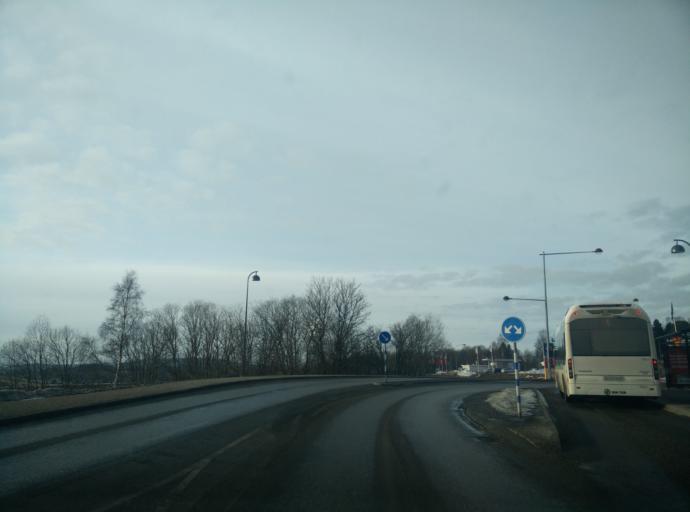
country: SE
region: Vaesternorrland
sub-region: Sundsvalls Kommun
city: Johannedal
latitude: 62.4309
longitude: 17.4160
